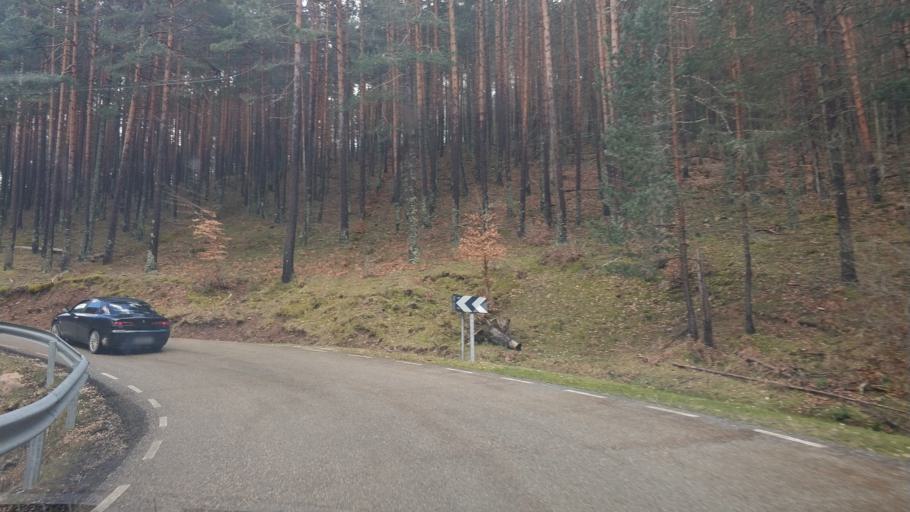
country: ES
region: Castille and Leon
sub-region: Provincia de Burgos
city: Neila
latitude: 42.0479
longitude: -3.0122
